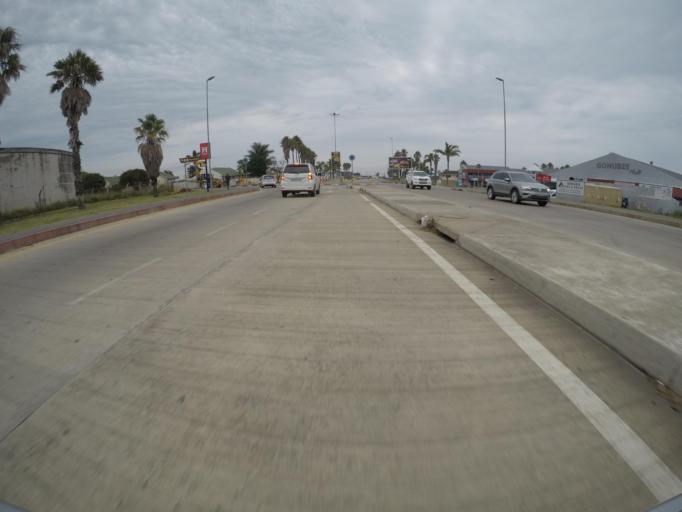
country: ZA
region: Eastern Cape
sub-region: Buffalo City Metropolitan Municipality
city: East London
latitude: -32.9349
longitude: 27.9951
